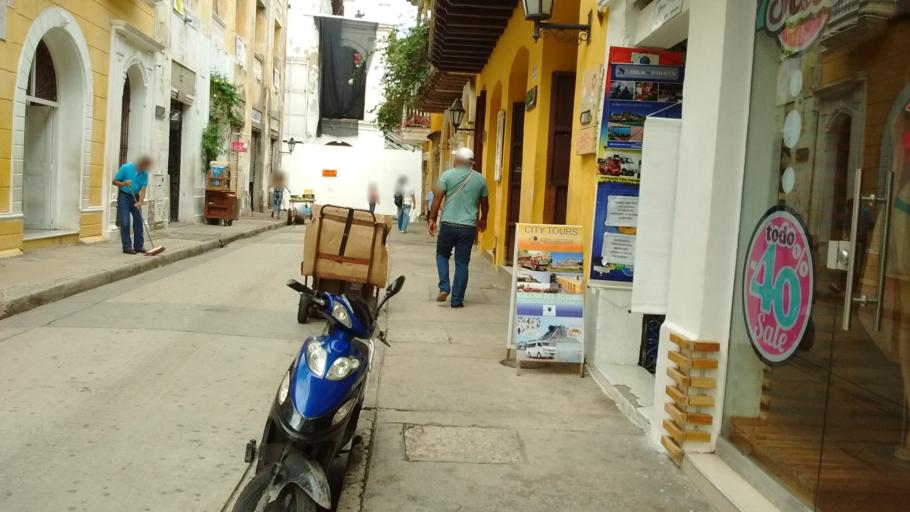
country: CO
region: Bolivar
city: Cartagena
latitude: 10.4234
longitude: -75.5499
